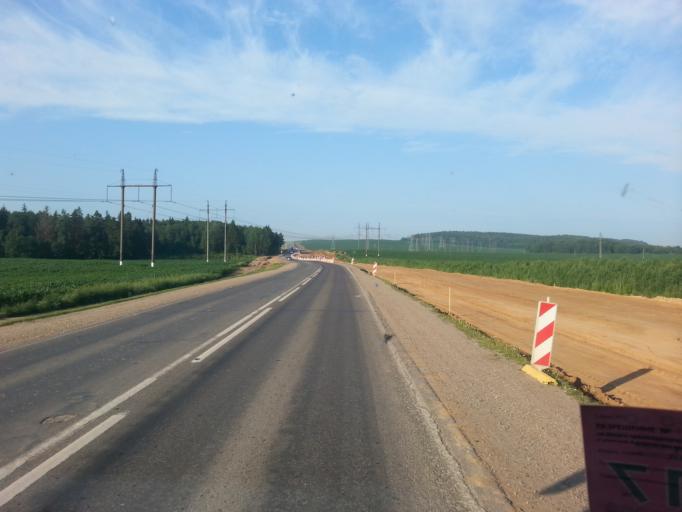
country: BY
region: Minsk
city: Bal'shavik
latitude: 54.0226
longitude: 27.5545
